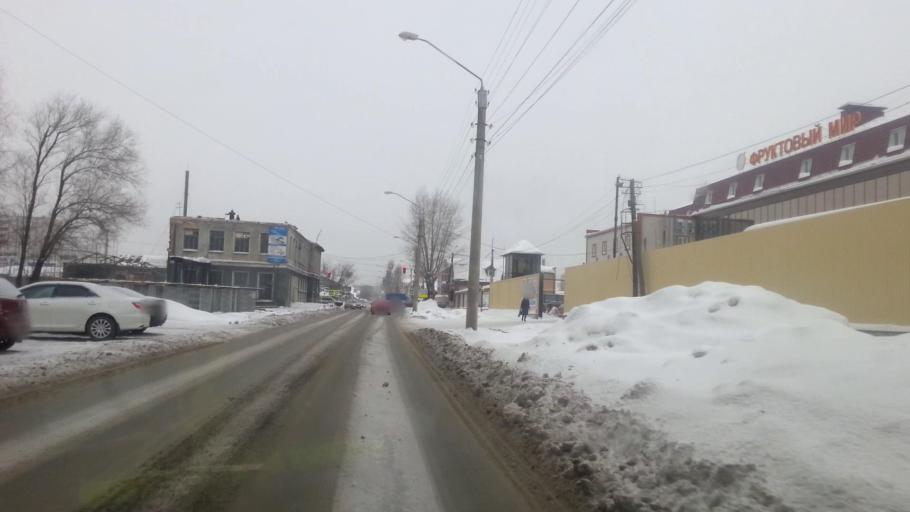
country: RU
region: Altai Krai
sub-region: Gorod Barnaulskiy
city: Barnaul
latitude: 53.3306
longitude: 83.7619
